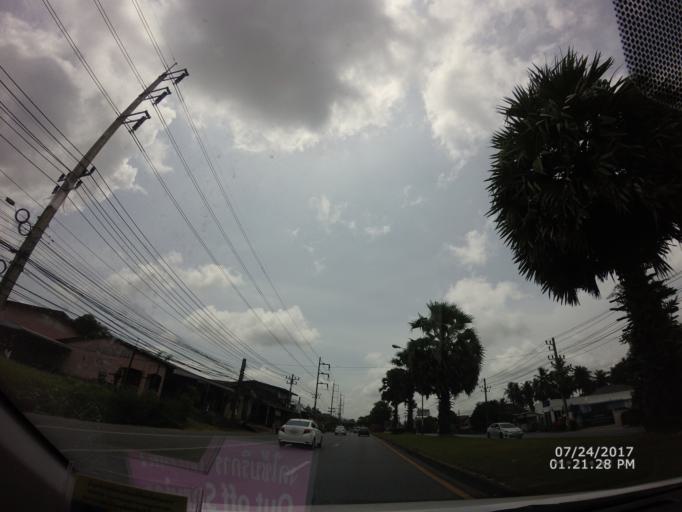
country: TH
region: Phuket
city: Thalang
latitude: 8.0838
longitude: 98.3426
